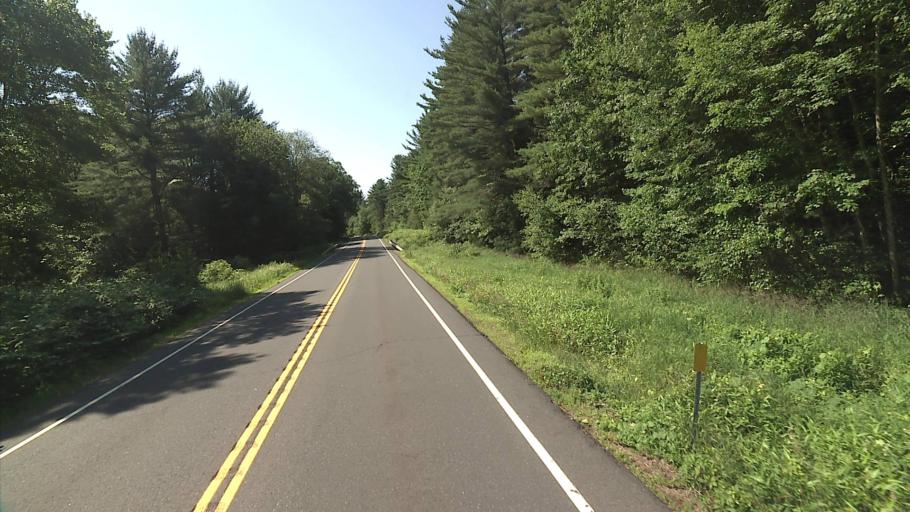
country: US
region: Connecticut
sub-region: Litchfield County
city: Terryville
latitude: 41.7063
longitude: -73.0099
